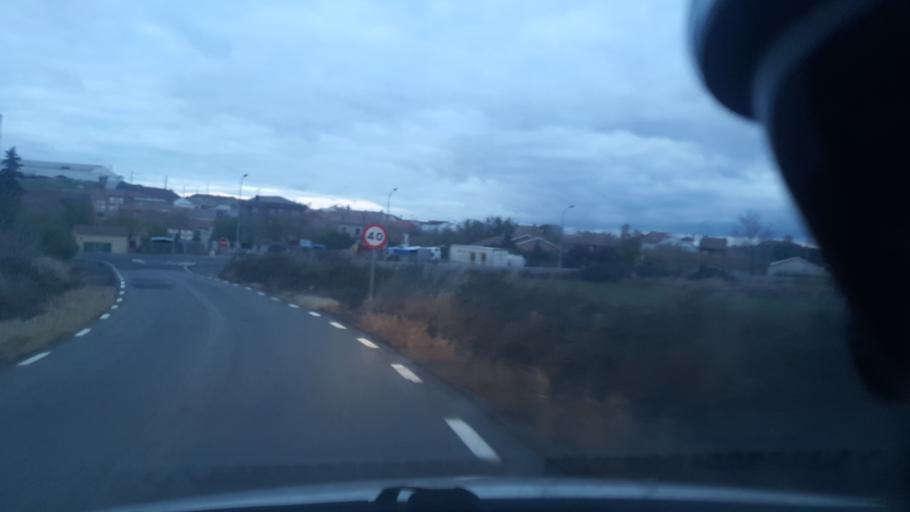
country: ES
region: Castille and Leon
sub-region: Provincia de Avila
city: Ojos-Albos
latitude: 40.7410
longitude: -4.4711
